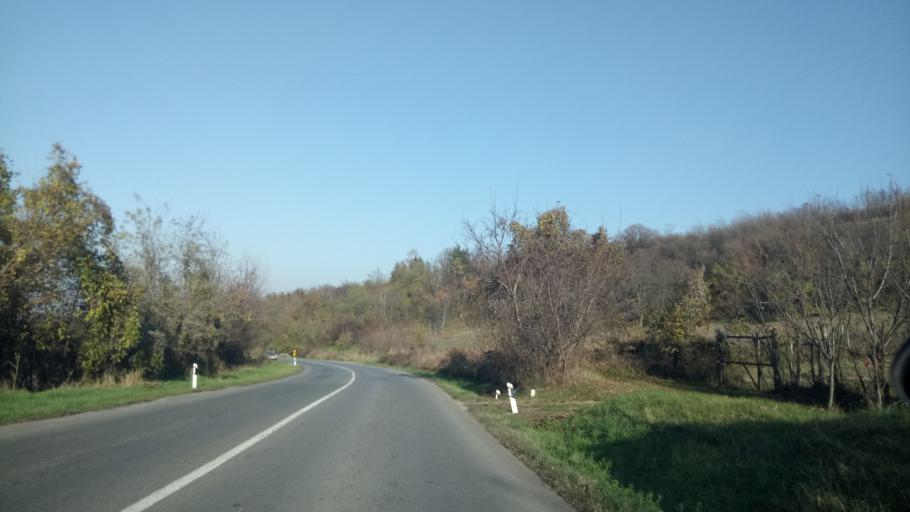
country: RS
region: Autonomna Pokrajina Vojvodina
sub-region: Juznobacki Okrug
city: Sremski Karlovci
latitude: 45.1751
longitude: 19.9513
